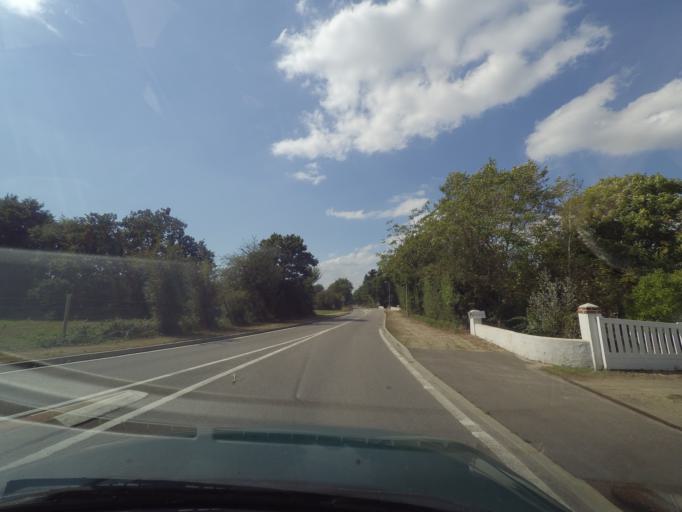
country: FR
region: Pays de la Loire
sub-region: Departement de la Loire-Atlantique
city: Saint-Hilaire-de-Chaleons
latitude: 47.1049
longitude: -1.8723
